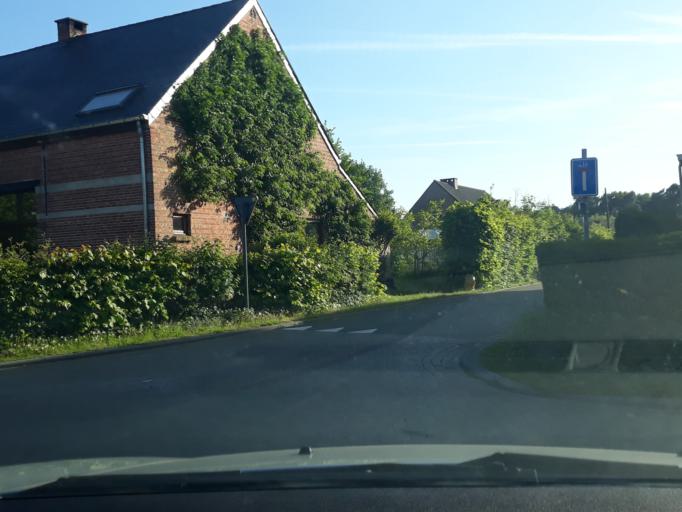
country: BE
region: Flanders
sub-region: Provincie Antwerpen
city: Grobbendonk
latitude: 51.1985
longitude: 4.7319
